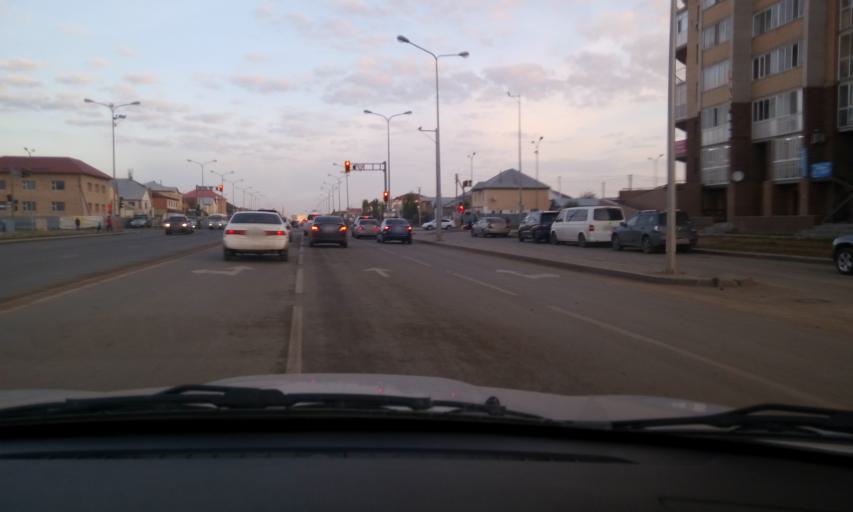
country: KZ
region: Astana Qalasy
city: Astana
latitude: 51.1307
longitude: 71.4962
